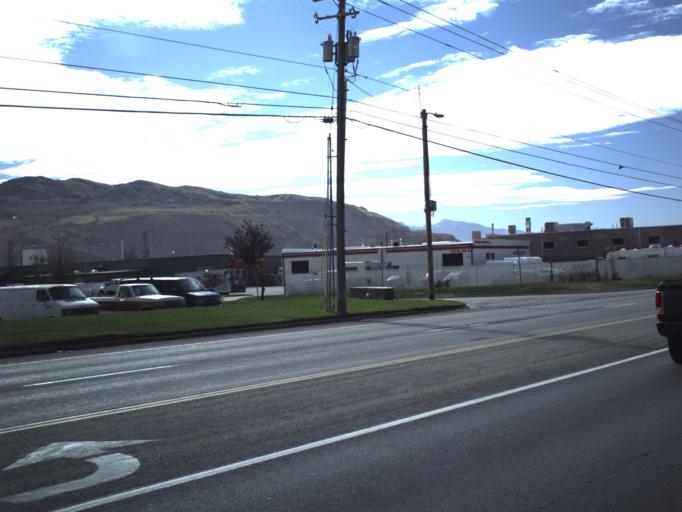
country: US
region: Utah
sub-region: Davis County
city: North Salt Lake
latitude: 40.8466
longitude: -111.9300
